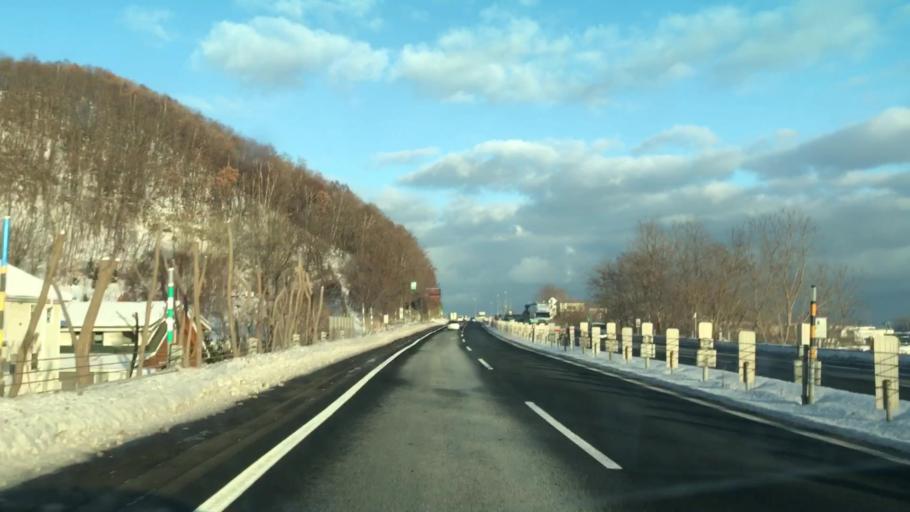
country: JP
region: Hokkaido
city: Sapporo
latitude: 43.1058
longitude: 141.2427
